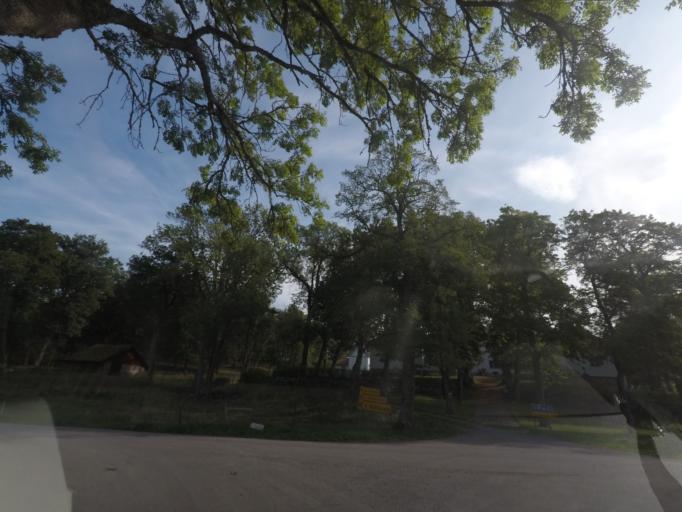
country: SE
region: Vaestmanland
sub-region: Kungsors Kommun
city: Kungsoer
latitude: 59.4837
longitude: 16.1786
